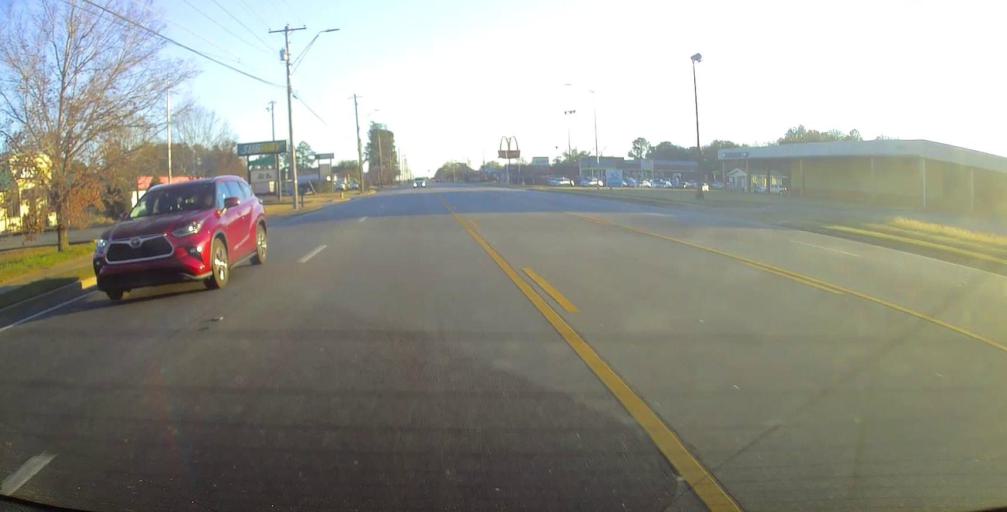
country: US
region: Georgia
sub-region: Dougherty County
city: Albany
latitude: 31.5645
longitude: -84.1763
